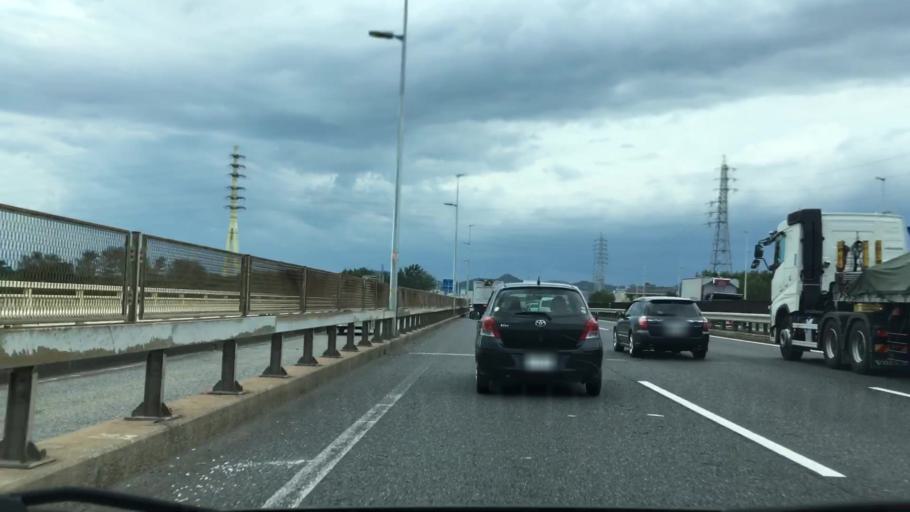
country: JP
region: Hyogo
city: Himeji
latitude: 34.8075
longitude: 134.6958
